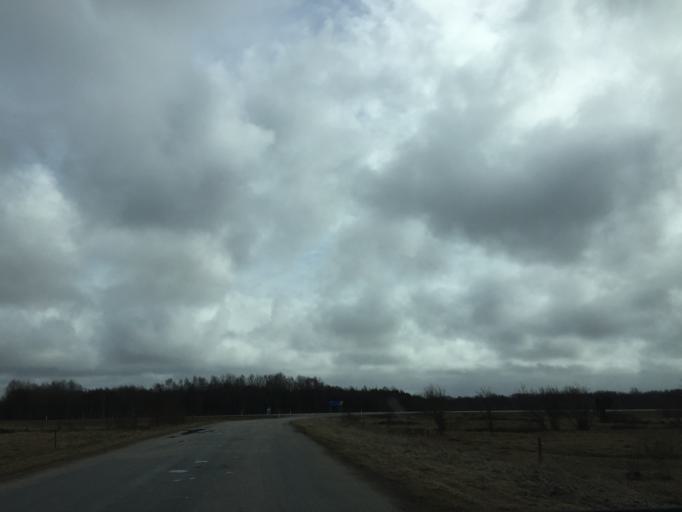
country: EE
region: Laeaene
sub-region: Lihula vald
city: Lihula
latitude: 58.7252
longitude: 23.9149
